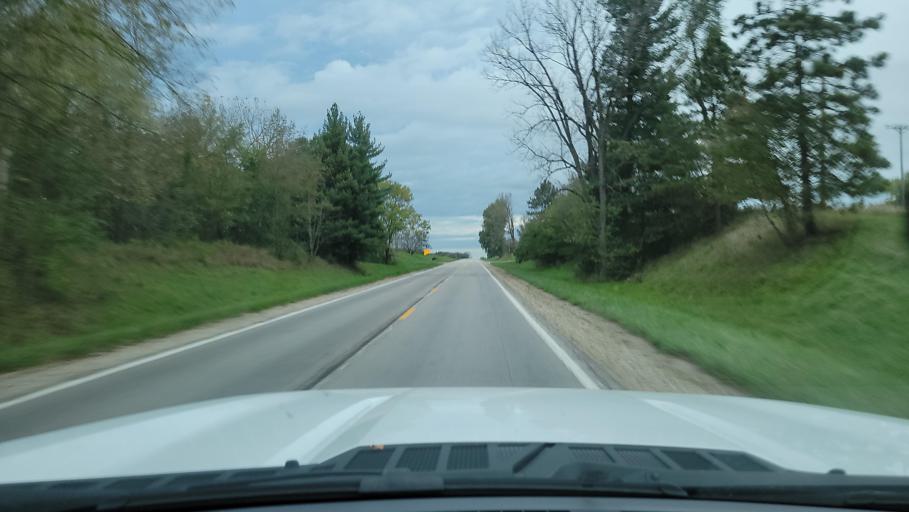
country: US
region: Illinois
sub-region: Schuyler County
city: Rushville
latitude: 40.0454
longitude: -90.6152
